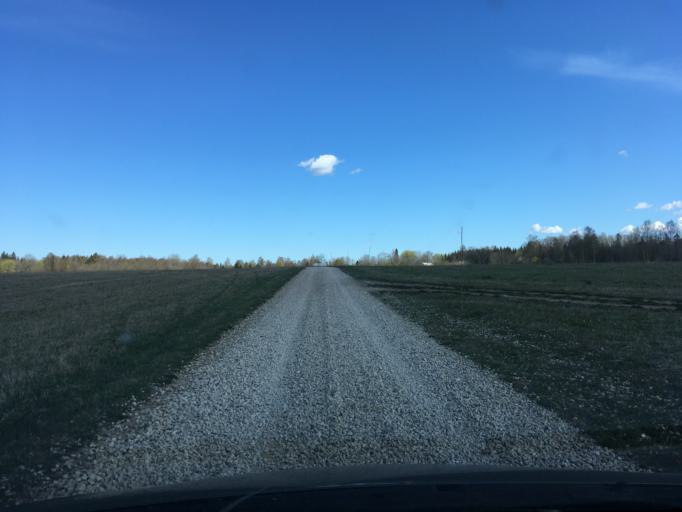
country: EE
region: Harju
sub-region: Raasiku vald
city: Raasiku
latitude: 59.2206
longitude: 25.2122
